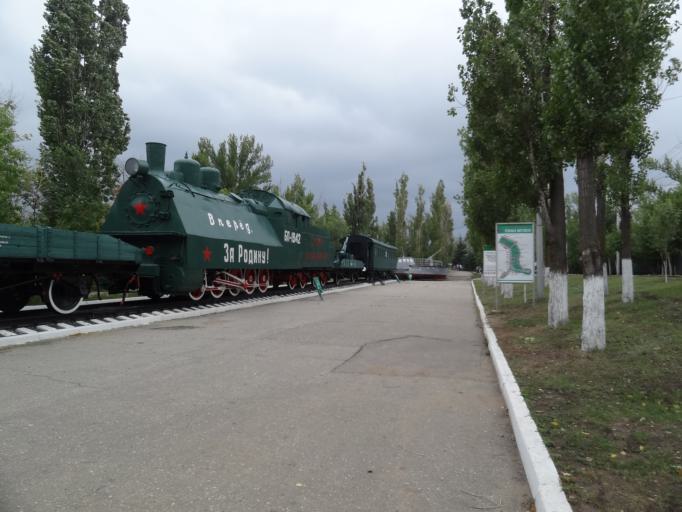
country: RU
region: Saratov
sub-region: Saratovskiy Rayon
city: Saratov
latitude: 51.5464
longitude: 46.0531
